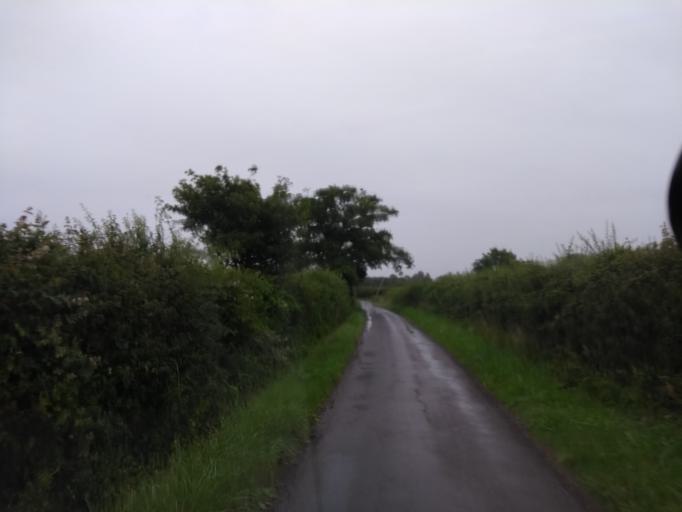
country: GB
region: England
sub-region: Somerset
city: Street
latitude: 51.0972
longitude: -2.6957
